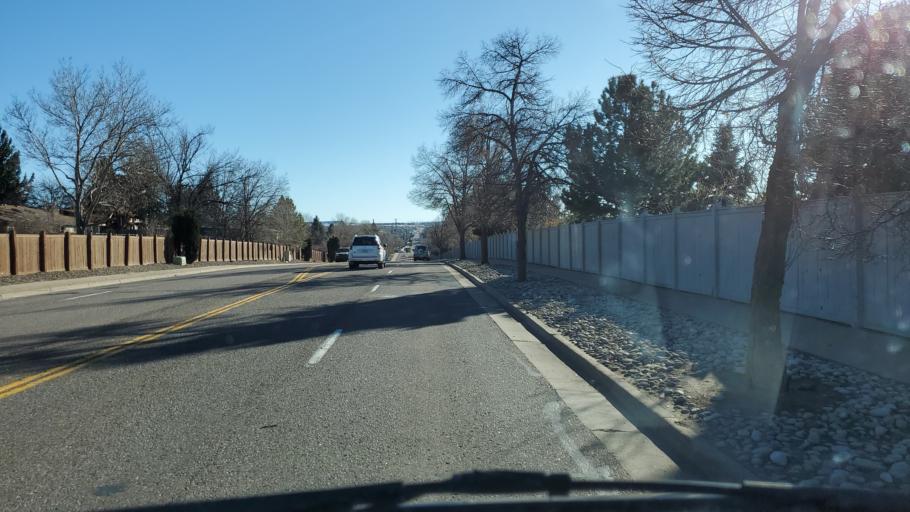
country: US
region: Colorado
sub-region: Arapahoe County
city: Castlewood
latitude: 39.5856
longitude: -104.9043
